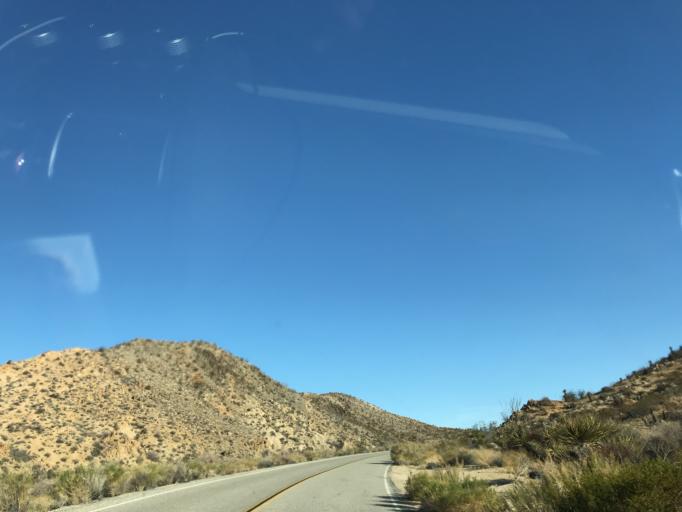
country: US
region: California
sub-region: Riverside County
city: Mecca
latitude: 33.7354
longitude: -115.8233
